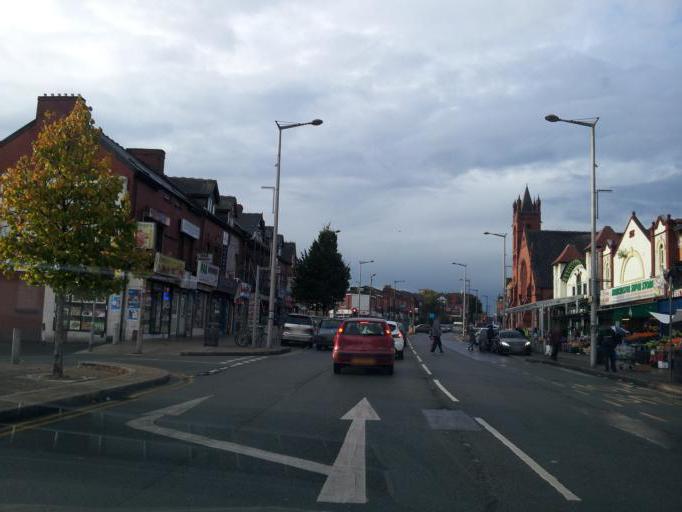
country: GB
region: England
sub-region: Manchester
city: Cheetham Hill
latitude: 53.5077
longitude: -2.2408
